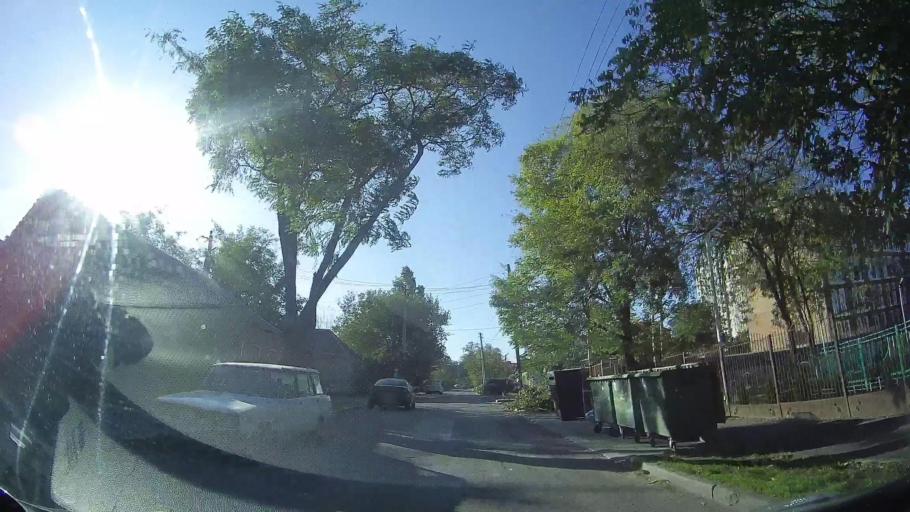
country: RU
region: Rostov
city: Rostov-na-Donu
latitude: 47.2132
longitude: 39.6836
